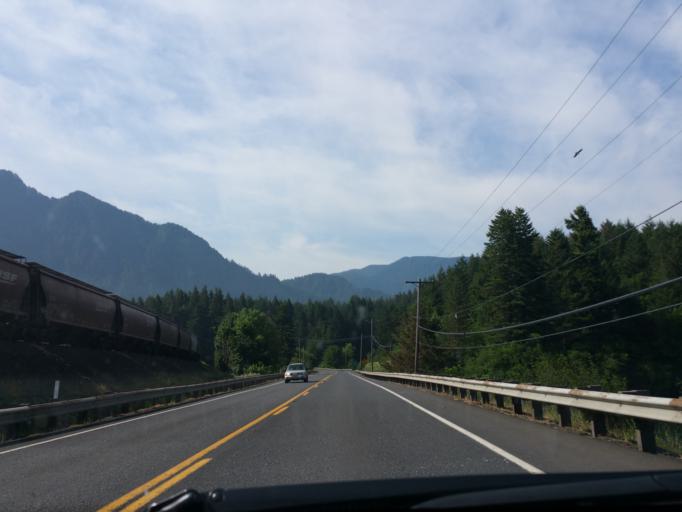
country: US
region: Oregon
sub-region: Hood River County
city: Cascade Locks
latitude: 45.6740
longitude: -121.9098
